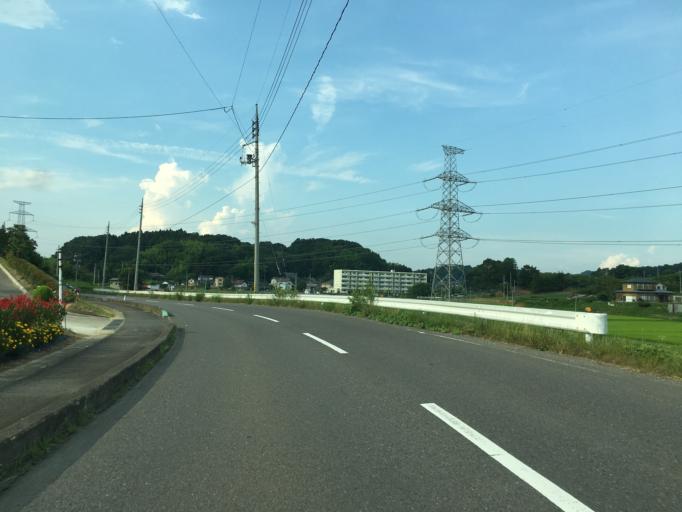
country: JP
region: Fukushima
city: Motomiya
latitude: 37.5038
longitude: 140.4335
